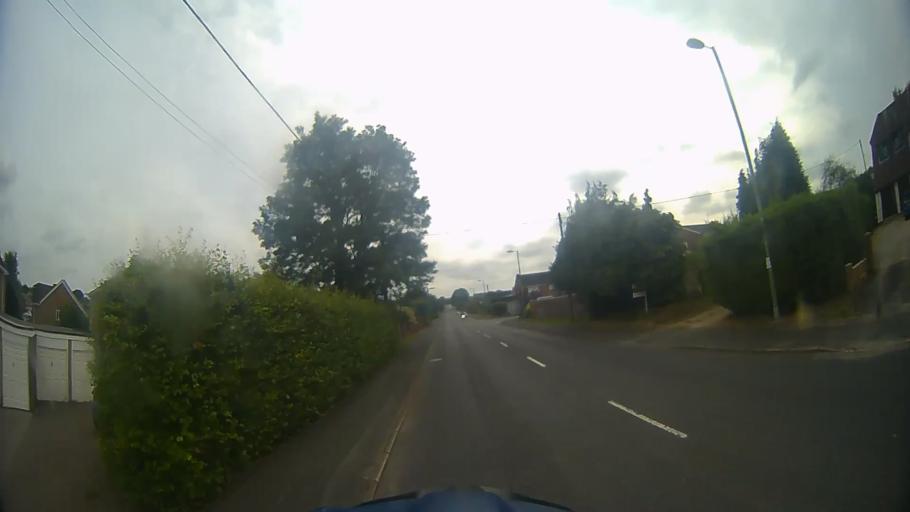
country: GB
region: England
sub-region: Hampshire
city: Basingstoke
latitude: 51.2515
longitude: -1.1386
